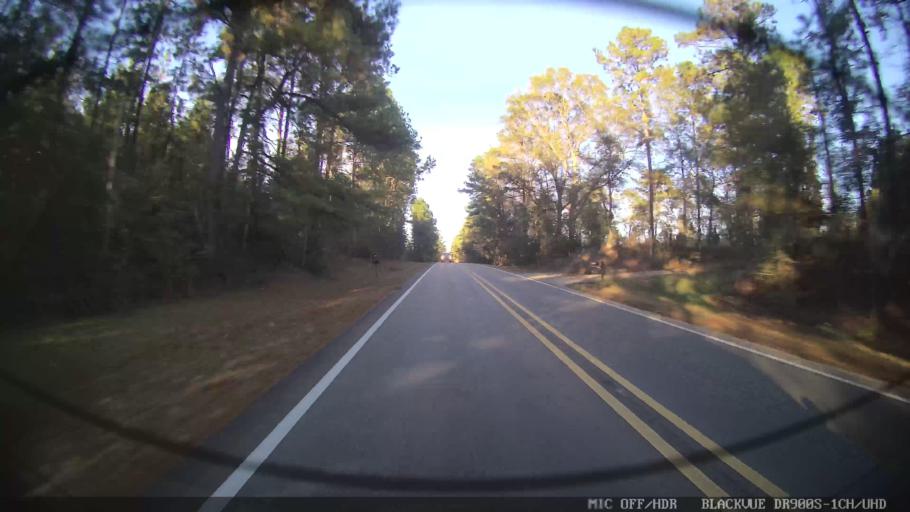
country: US
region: Mississippi
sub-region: Lamar County
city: Lumberton
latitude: 31.0541
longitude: -89.4301
